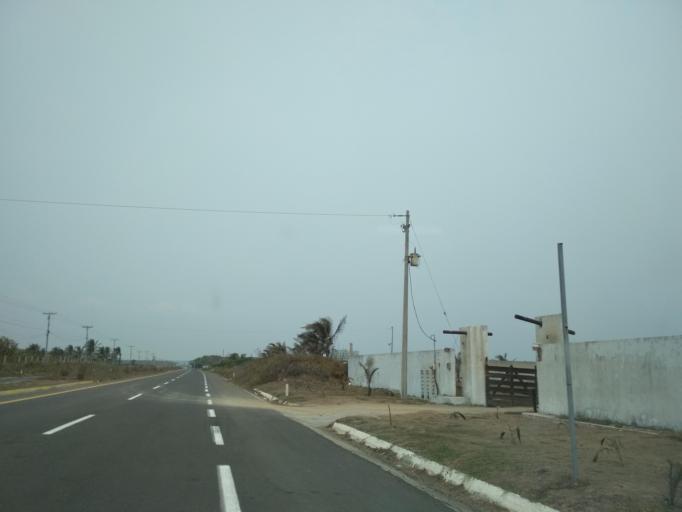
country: MX
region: Veracruz
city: Anton Lizardo
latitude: 19.0526
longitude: -96.0220
